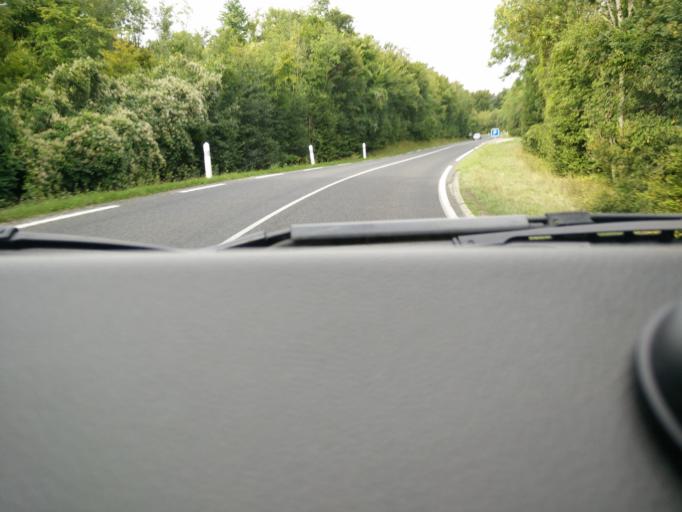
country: FR
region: Lorraine
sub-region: Departement de Meurthe-et-Moselle
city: Montauville
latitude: 48.8993
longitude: 5.9934
